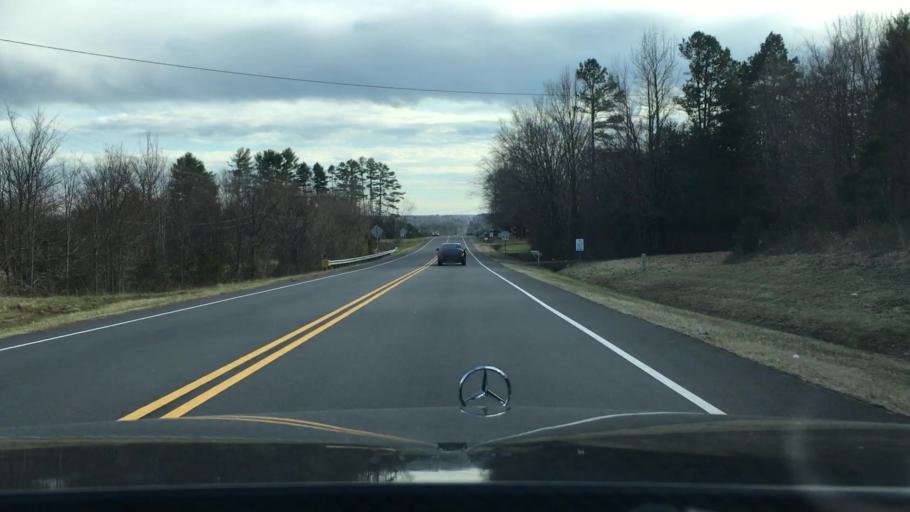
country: US
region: Virginia
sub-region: City of Danville
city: Danville
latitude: 36.5263
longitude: -79.3972
